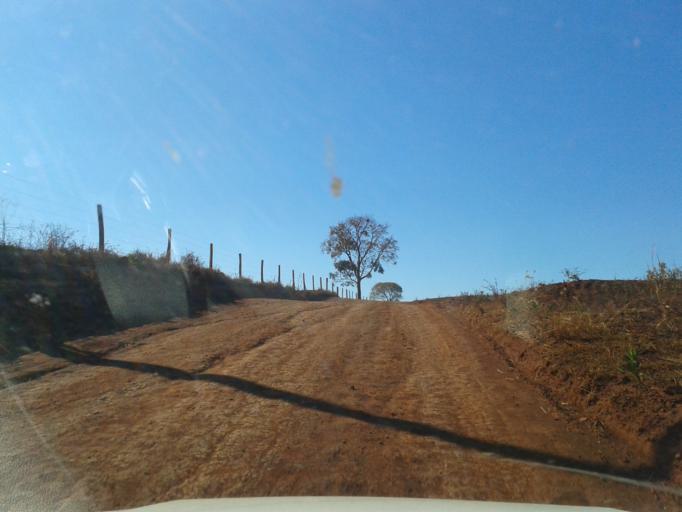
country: BR
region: Minas Gerais
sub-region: Centralina
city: Centralina
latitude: -18.5904
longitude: -49.1755
